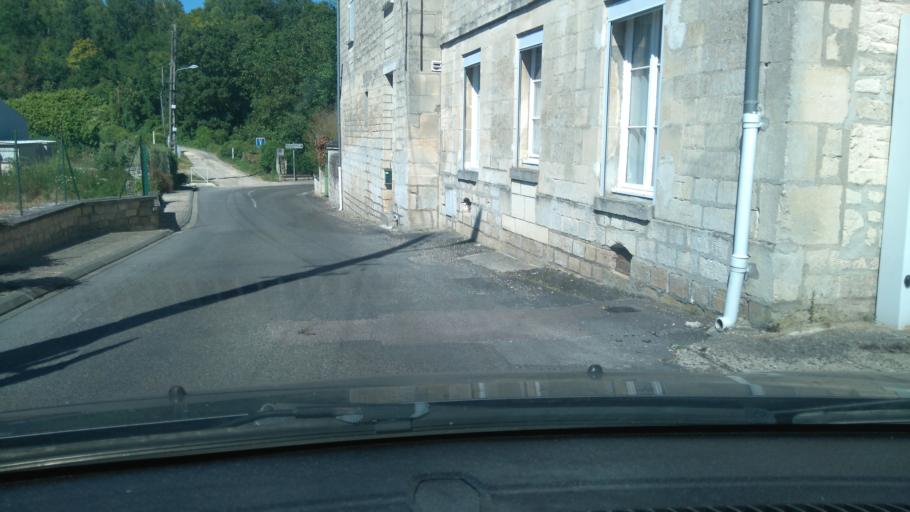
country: FR
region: Picardie
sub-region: Departement de l'Oise
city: Saint-Maximin
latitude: 49.2257
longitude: 2.4432
